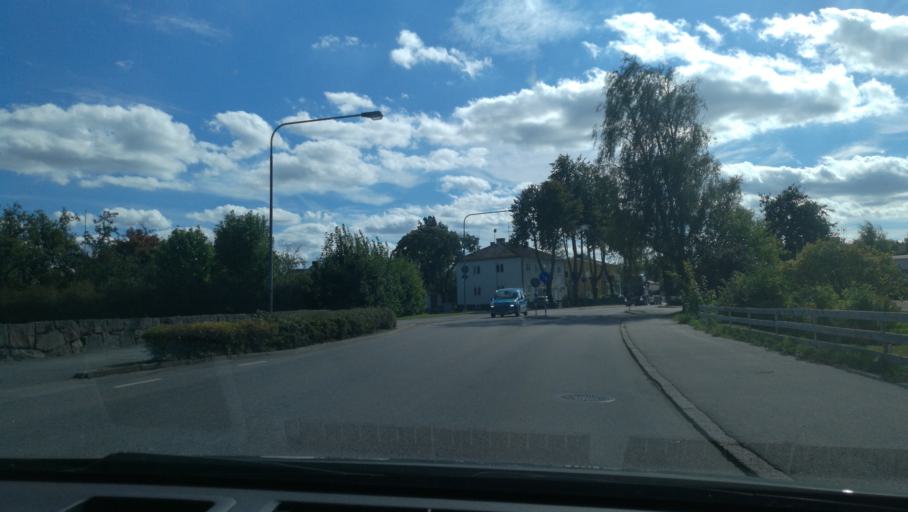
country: SE
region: Vaestra Goetaland
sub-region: Mariestads Kommun
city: Mariestad
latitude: 58.7015
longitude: 13.8366
